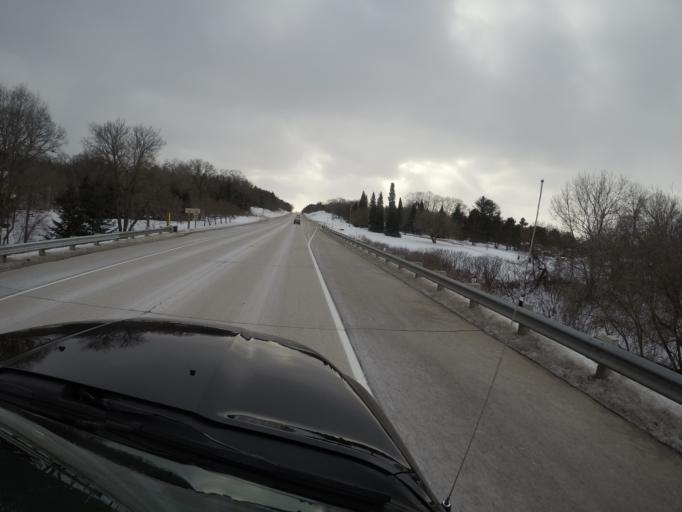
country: US
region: Wisconsin
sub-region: Trempealeau County
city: Galesville
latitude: 44.0607
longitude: -91.2911
